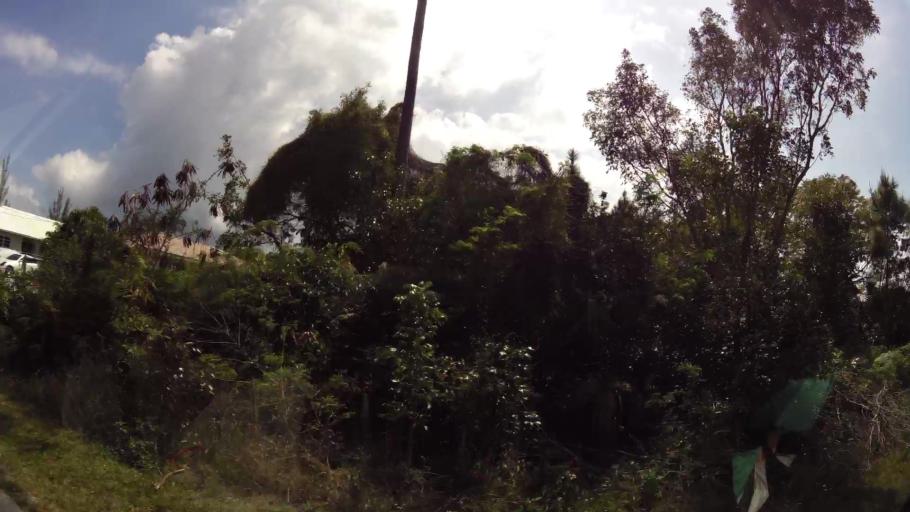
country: BS
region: Freeport
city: Freeport
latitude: 26.5022
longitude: -78.7054
